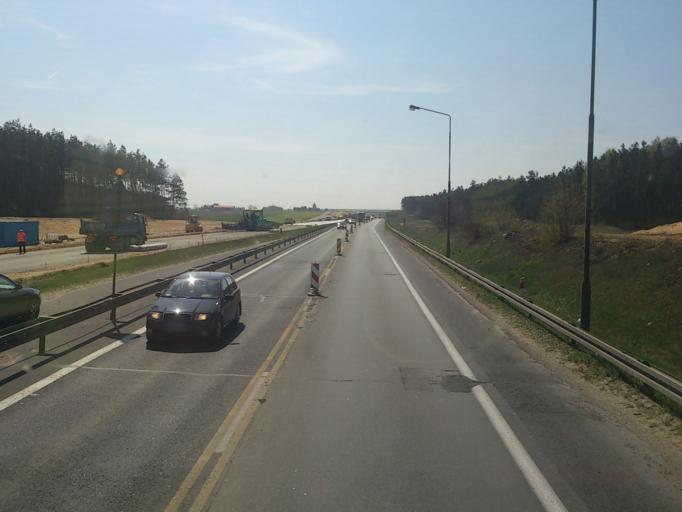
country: PL
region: Lodz Voivodeship
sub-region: Powiat piotrkowski
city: Czarnocin
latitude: 51.5433
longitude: 19.6026
